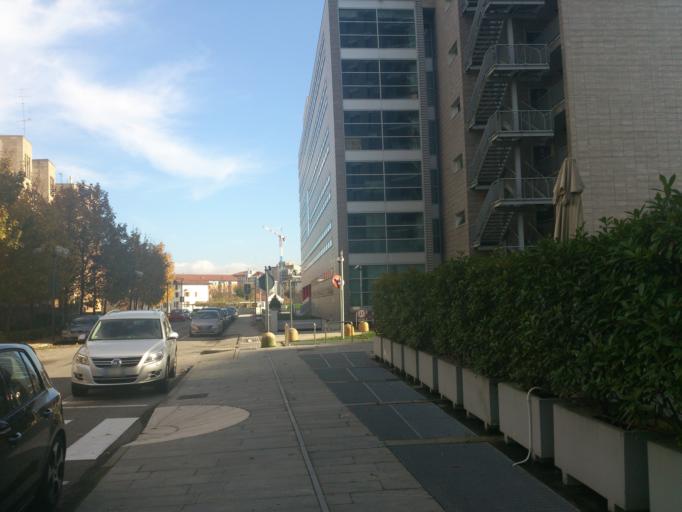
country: IT
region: Lombardy
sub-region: Citta metropolitana di Milano
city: San Donato Milanese
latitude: 45.4180
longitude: 9.2575
